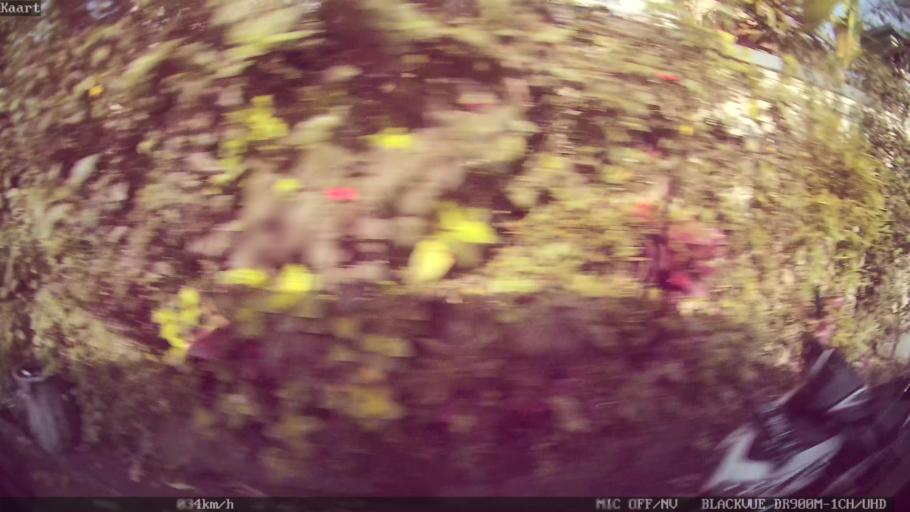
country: ID
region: Bali
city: Banjar Pande
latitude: -8.5182
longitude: 115.2501
